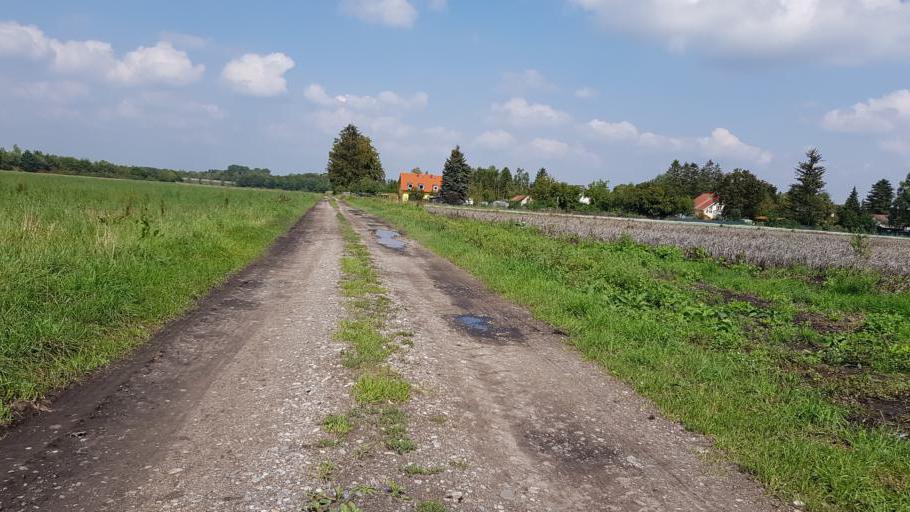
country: DE
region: Bavaria
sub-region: Upper Bavaria
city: Karlsfeld
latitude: 48.2070
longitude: 11.4998
